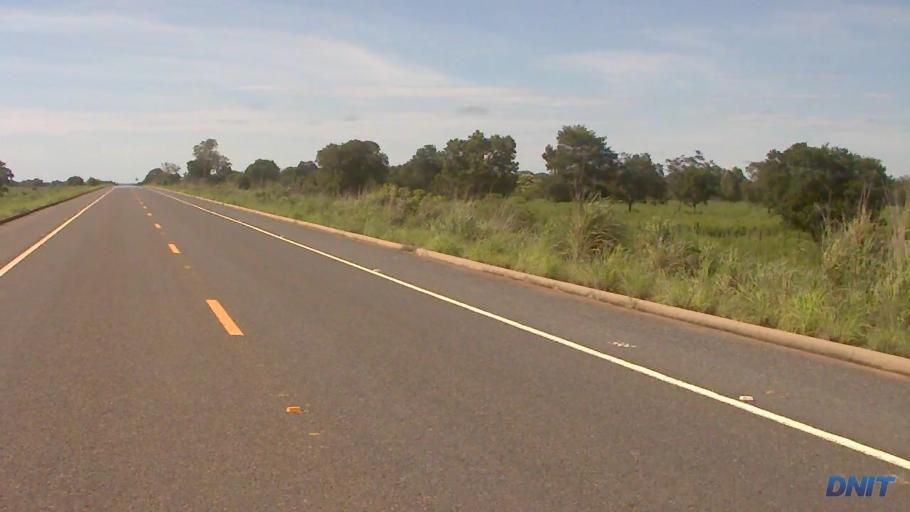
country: BR
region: Goias
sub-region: Sao Miguel Do Araguaia
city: Sao Miguel do Araguaia
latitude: -13.4307
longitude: -50.1264
